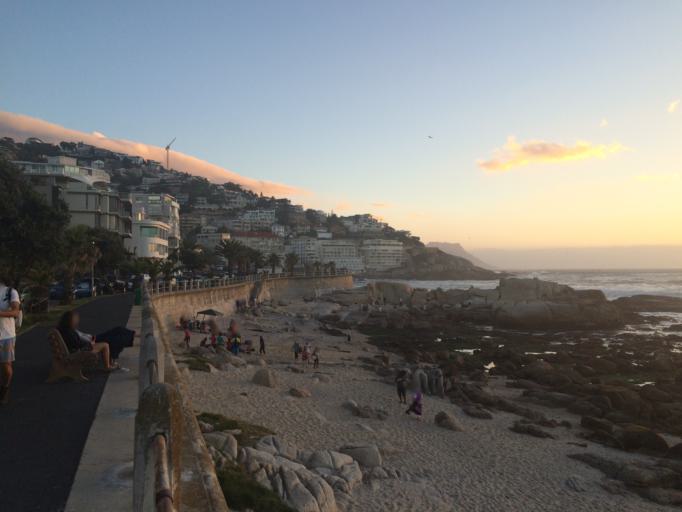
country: ZA
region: Western Cape
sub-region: City of Cape Town
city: Cape Town
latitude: -33.9233
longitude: 18.3777
